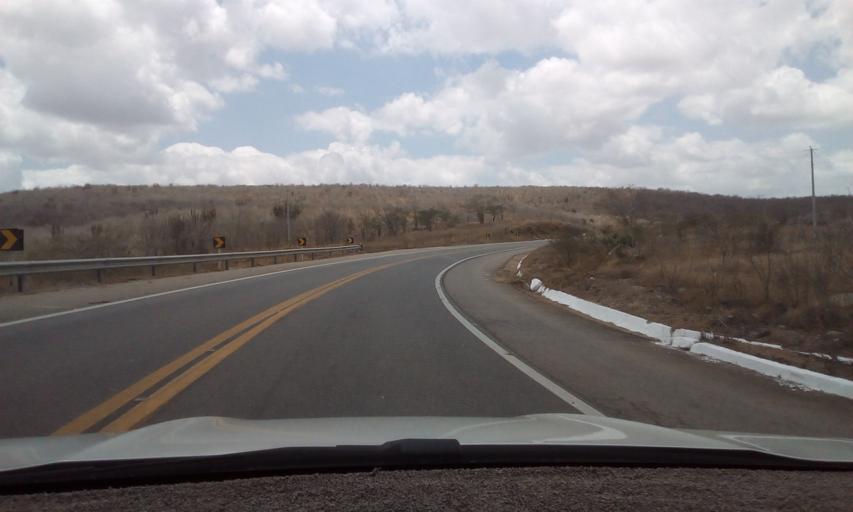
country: BR
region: Paraiba
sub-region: Boqueirao
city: Boqueirao
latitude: -7.6806
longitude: -36.0602
